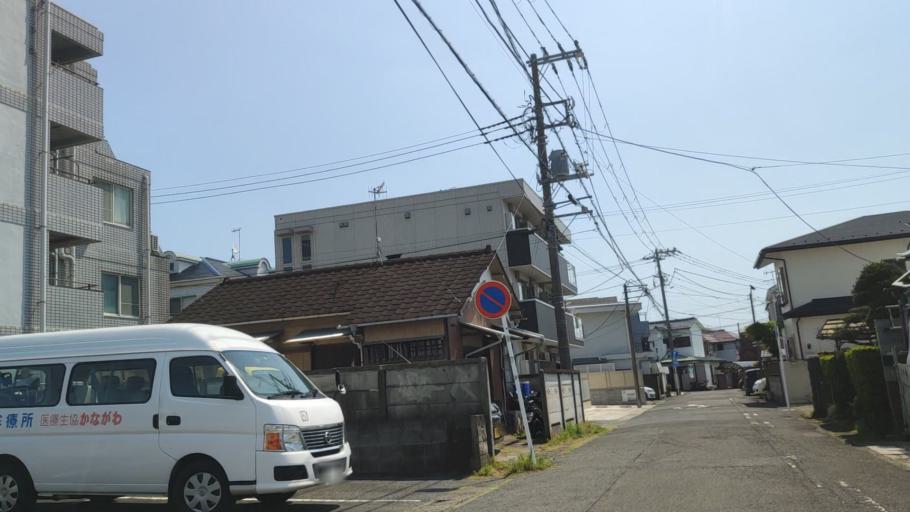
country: JP
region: Kanagawa
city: Hiratsuka
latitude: 35.3258
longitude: 139.3556
